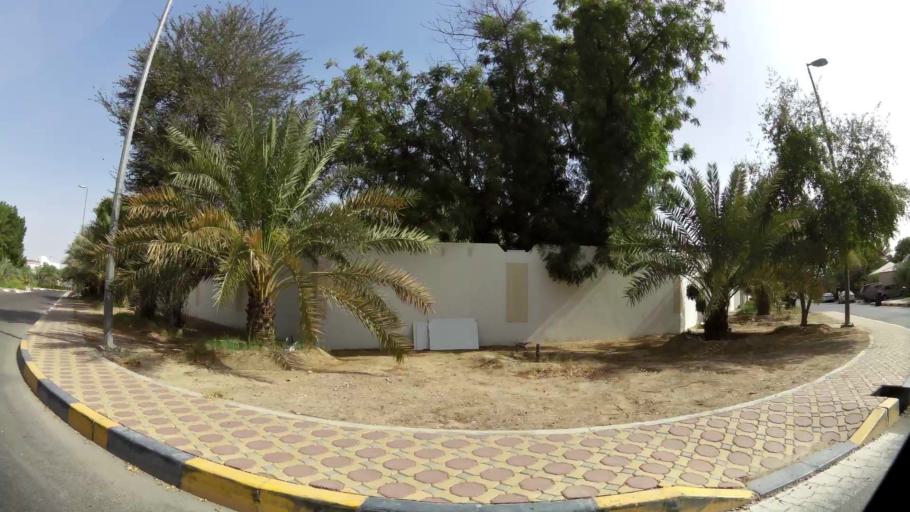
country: AE
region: Abu Dhabi
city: Al Ain
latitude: 24.2492
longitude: 55.6872
